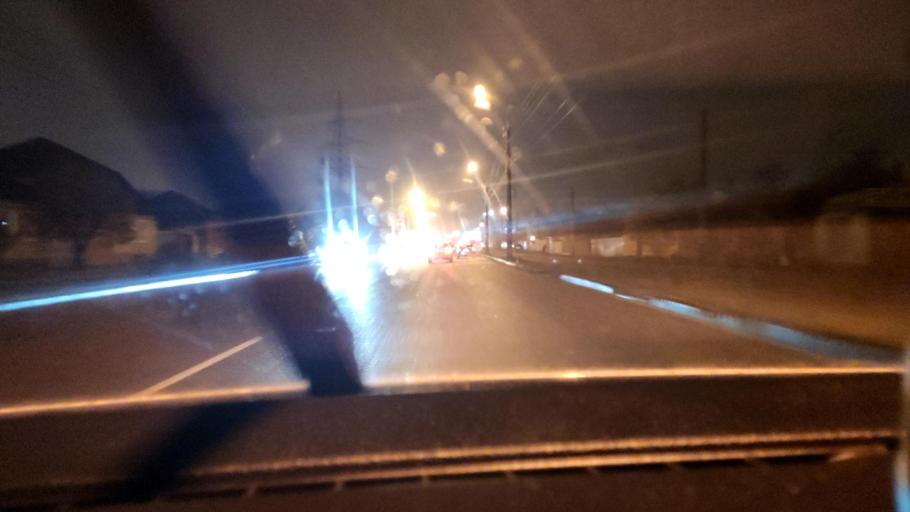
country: RU
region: Voronezj
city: Voronezh
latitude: 51.6420
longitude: 39.1565
